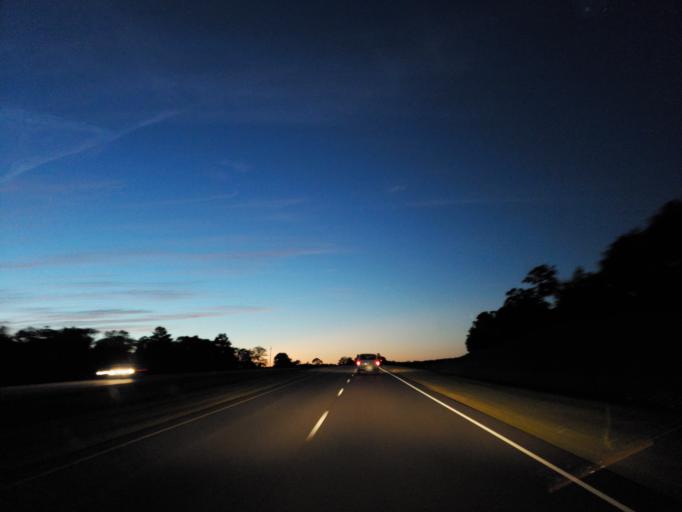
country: US
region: Mississippi
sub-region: Clarke County
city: Quitman
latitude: 32.1056
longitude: -88.7108
